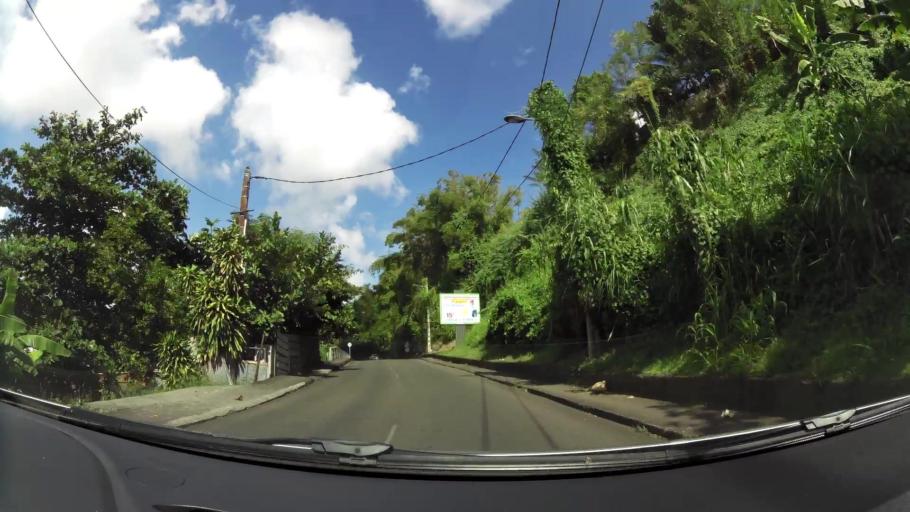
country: MQ
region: Martinique
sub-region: Martinique
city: Fort-de-France
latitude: 14.6071
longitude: -61.0619
